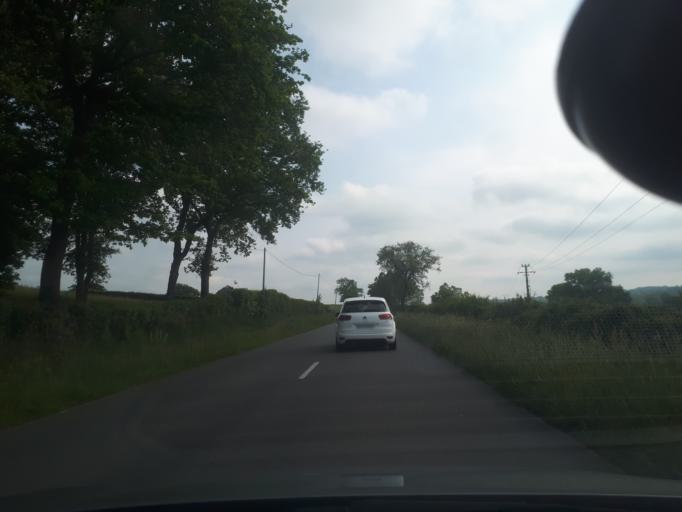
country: FR
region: Auvergne
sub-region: Departement de l'Allier
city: Lapalisse
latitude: 46.3919
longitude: 3.5916
